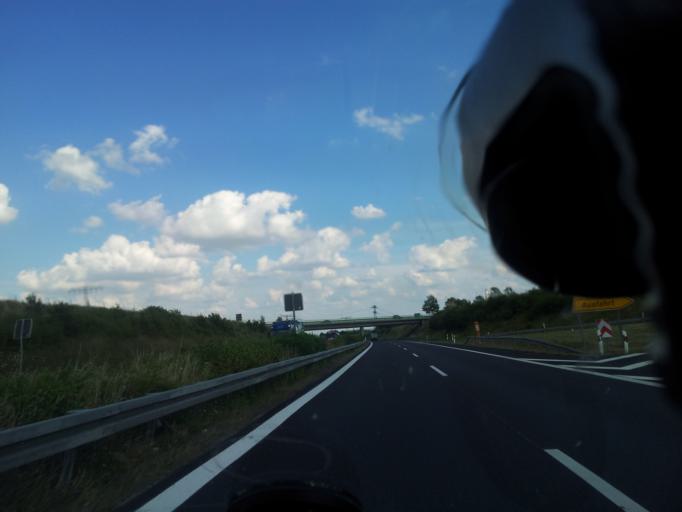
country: DE
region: Saxony-Anhalt
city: Blankenburg
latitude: 51.8129
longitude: 10.9395
